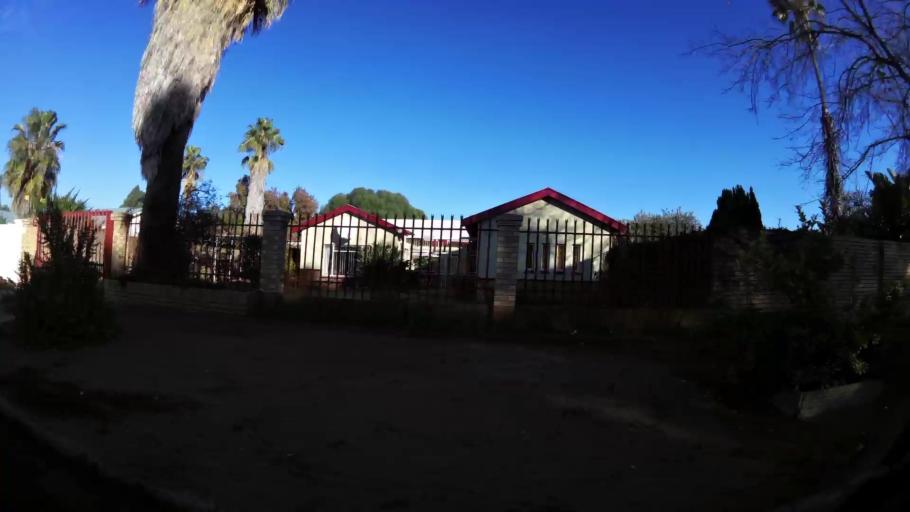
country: ZA
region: Northern Cape
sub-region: Frances Baard District Municipality
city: Kimberley
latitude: -28.7412
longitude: 24.7386
